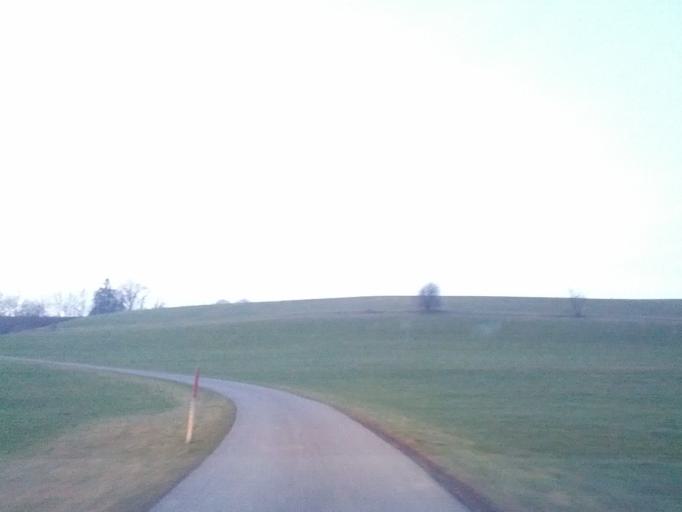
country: DE
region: Baden-Wuerttemberg
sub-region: Tuebingen Region
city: Steinhausen an der Rottum
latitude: 47.9810
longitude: 9.9872
